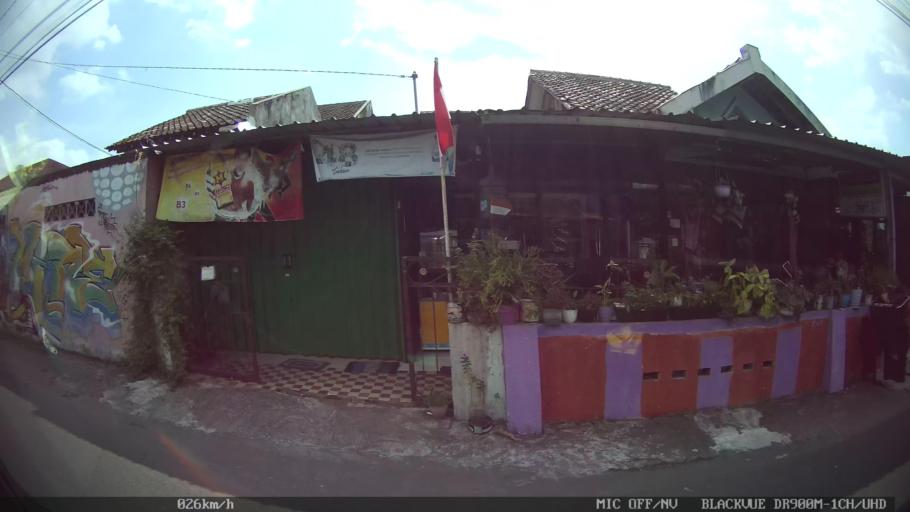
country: ID
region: Daerah Istimewa Yogyakarta
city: Gamping Lor
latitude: -7.8088
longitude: 110.3320
